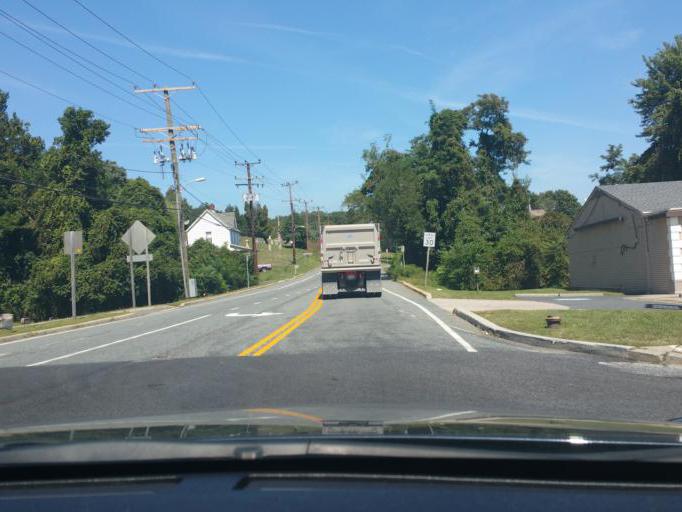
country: US
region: Maryland
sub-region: Harford County
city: Havre de Grace
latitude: 39.5541
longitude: -76.1021
